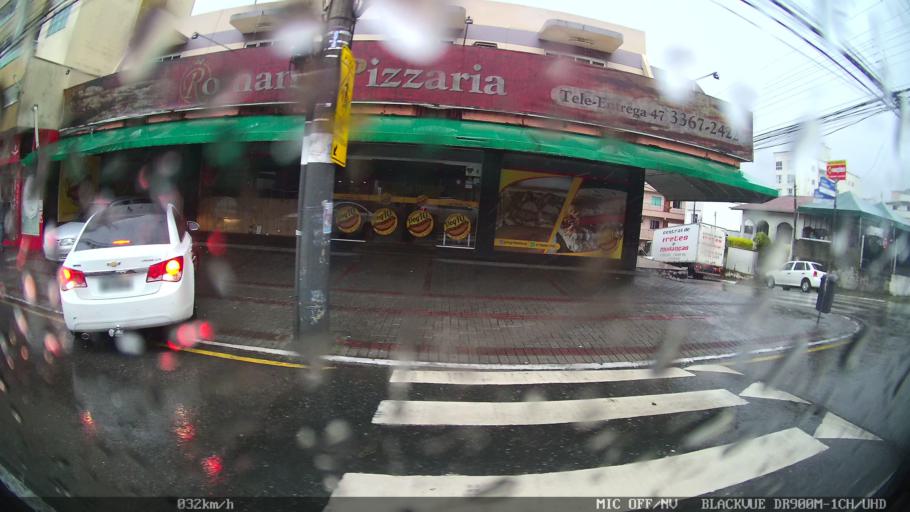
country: BR
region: Santa Catarina
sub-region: Balneario Camboriu
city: Balneario Camboriu
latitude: -26.9787
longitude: -48.6466
